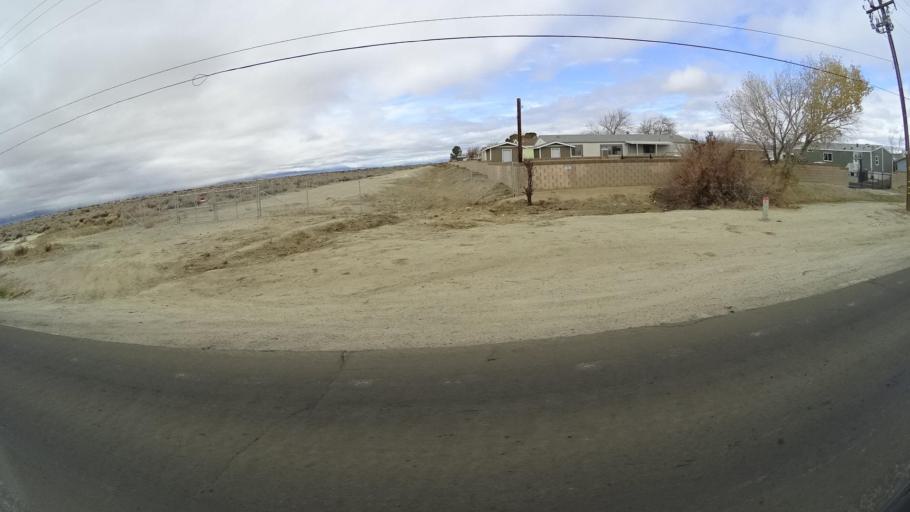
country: US
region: California
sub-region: Kern County
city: Rosamond
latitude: 34.8426
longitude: -118.1670
